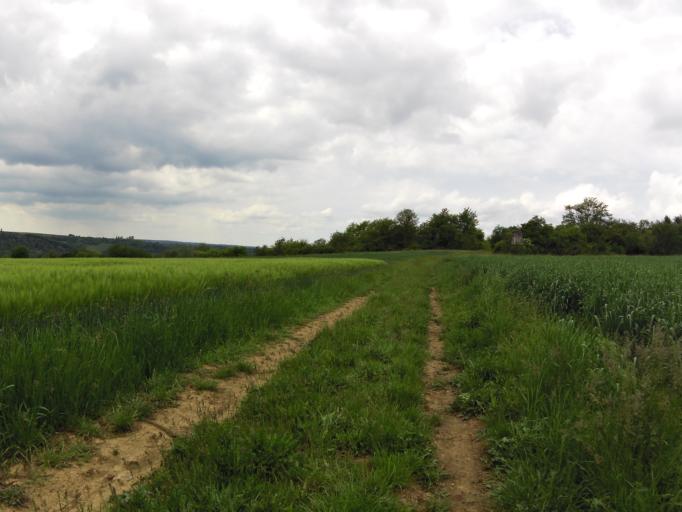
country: DE
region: Bavaria
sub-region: Regierungsbezirk Unterfranken
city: Winterhausen
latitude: 49.7147
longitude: 10.0239
